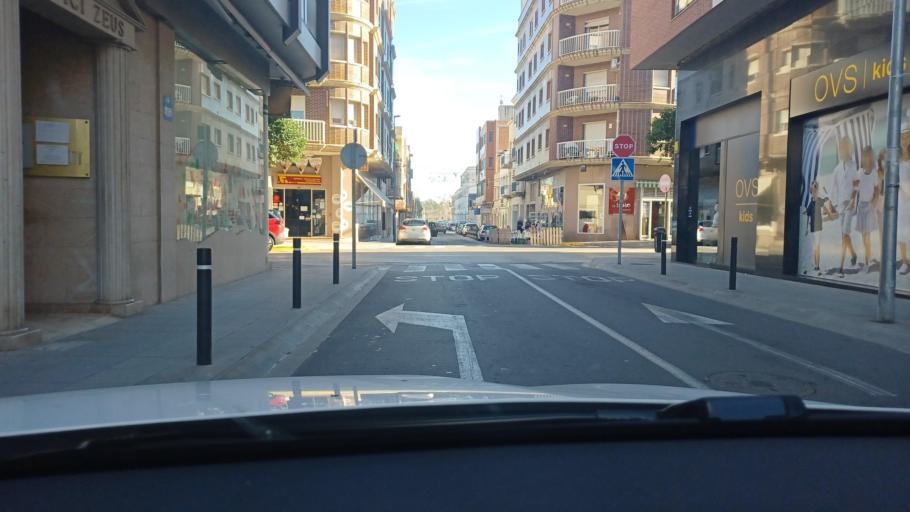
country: ES
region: Catalonia
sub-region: Provincia de Tarragona
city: Amposta
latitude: 40.7101
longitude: 0.5796
